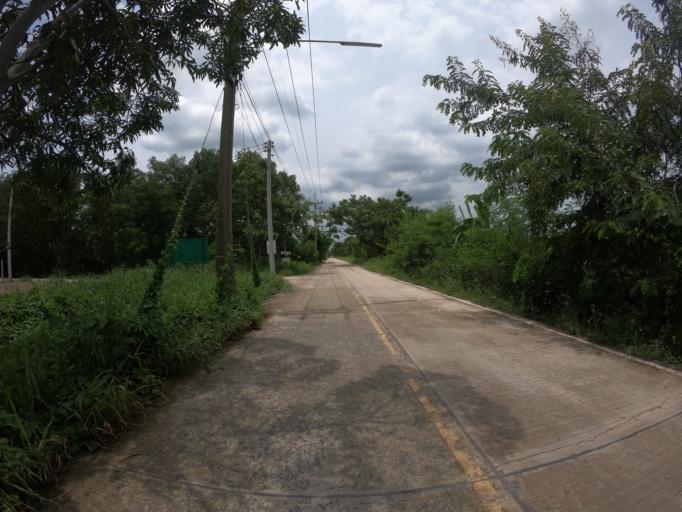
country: TH
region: Pathum Thani
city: Ban Lam Luk Ka
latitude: 13.9900
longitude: 100.8572
